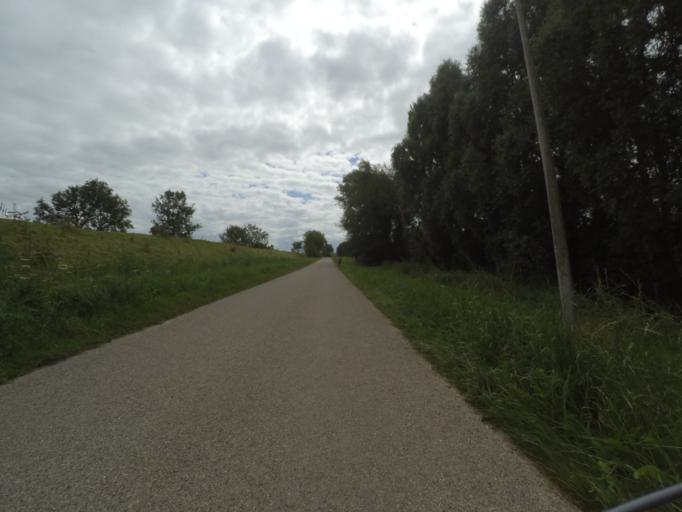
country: NL
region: Friesland
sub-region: Gemeente Kollumerland en Nieuwkruisland
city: Kollum
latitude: 53.3290
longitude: 6.1546
